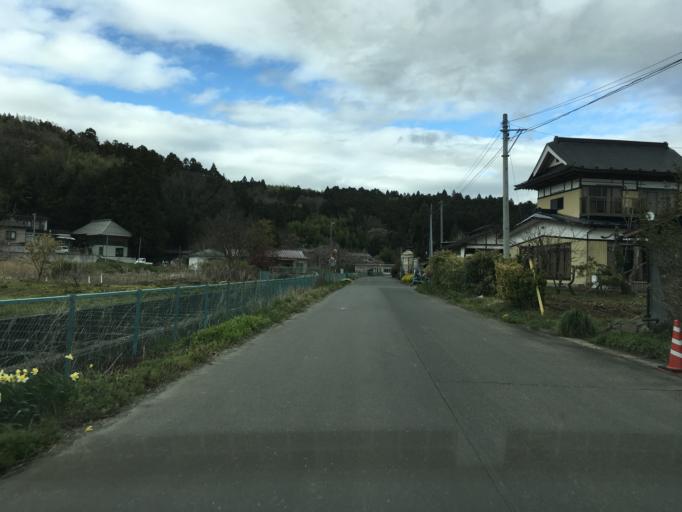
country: JP
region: Iwate
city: Ichinoseki
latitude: 38.7614
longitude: 141.2676
